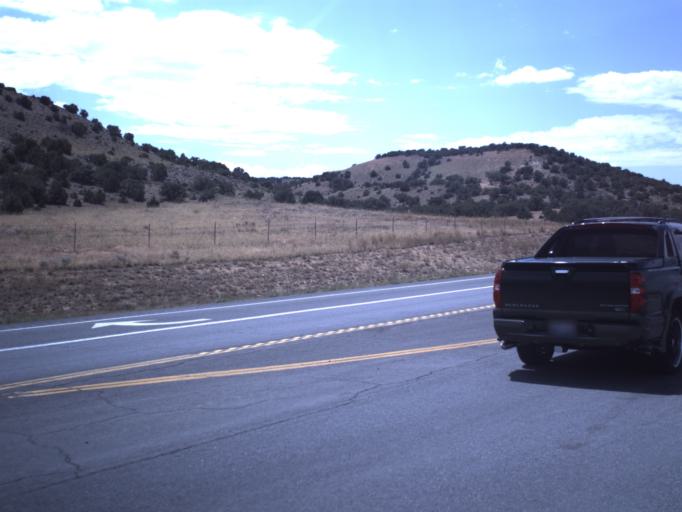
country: US
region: Utah
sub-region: Duchesne County
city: Duchesne
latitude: 40.1720
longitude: -110.3374
